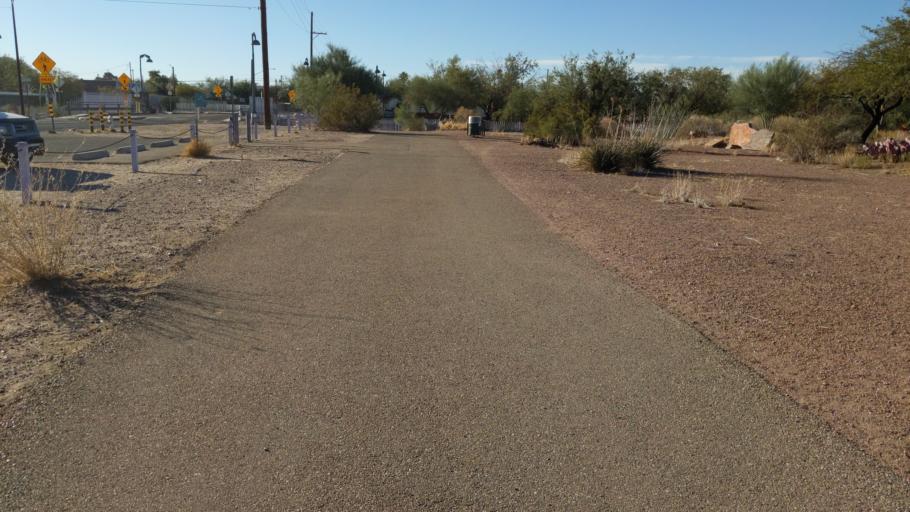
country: US
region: Arizona
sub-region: Pima County
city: South Tucson
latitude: 32.1898
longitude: -110.9778
